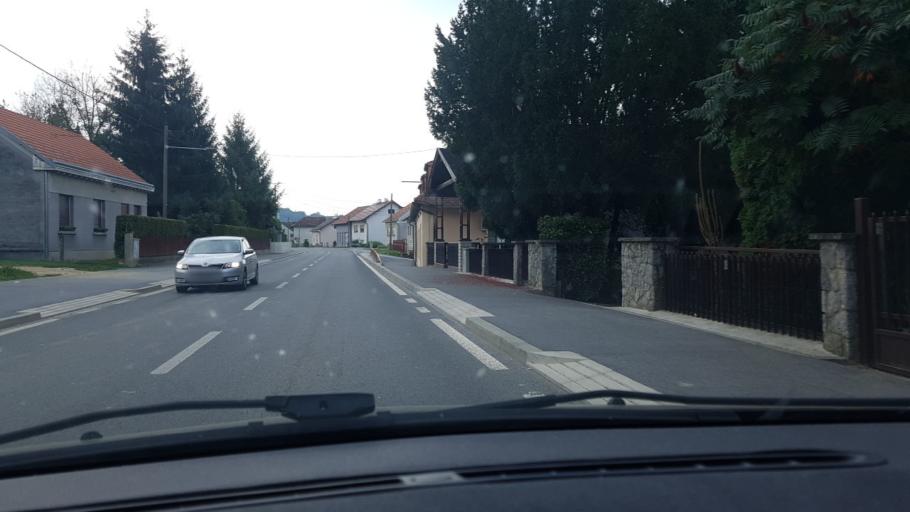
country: HR
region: Krapinsko-Zagorska
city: Zlatar
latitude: 46.0950
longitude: 16.0740
